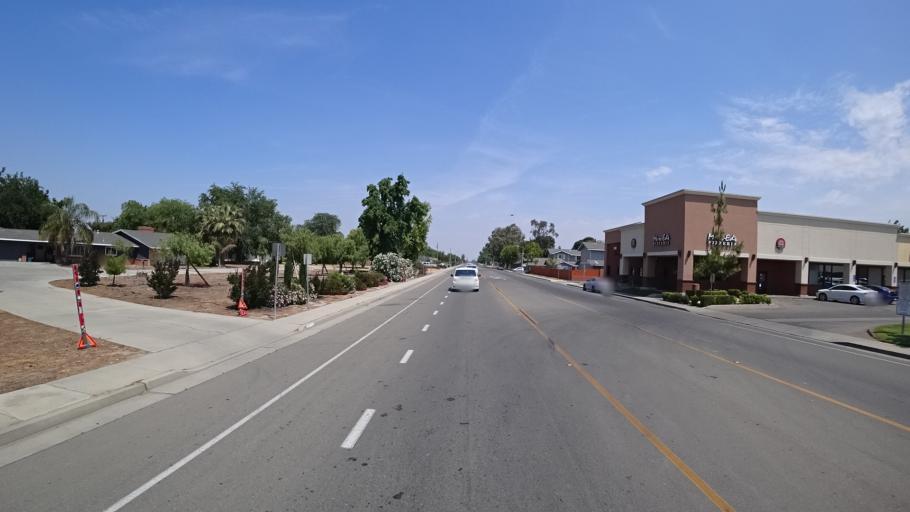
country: US
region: California
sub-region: Kings County
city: Lemoore
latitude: 36.3155
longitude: -119.7808
